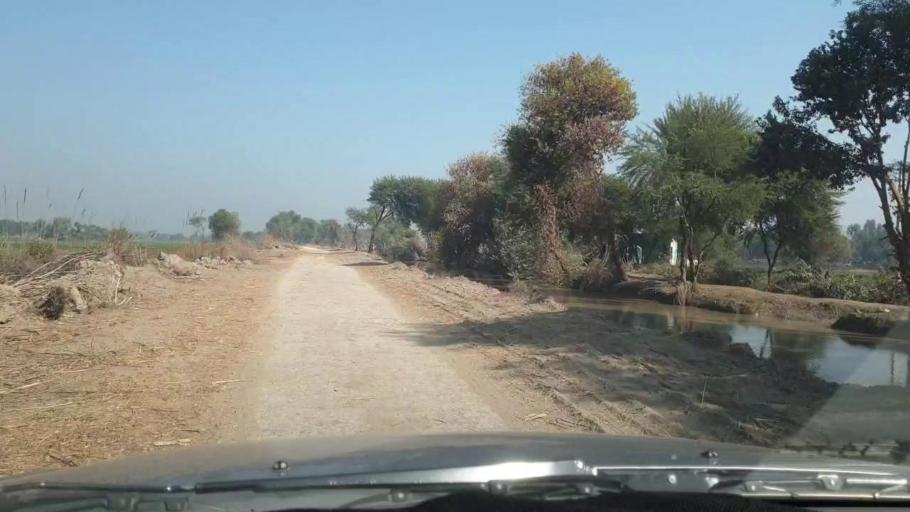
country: PK
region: Sindh
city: Khanpur
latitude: 27.7784
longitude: 69.5405
